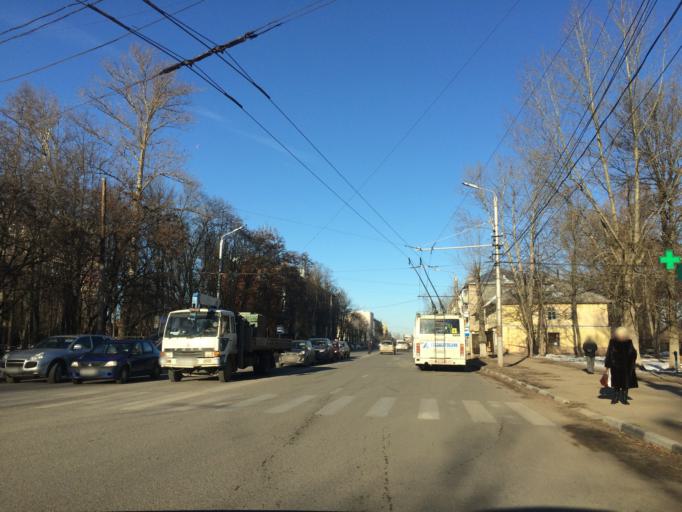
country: RU
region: Tula
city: Mendeleyevskiy
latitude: 54.1719
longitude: 37.5756
